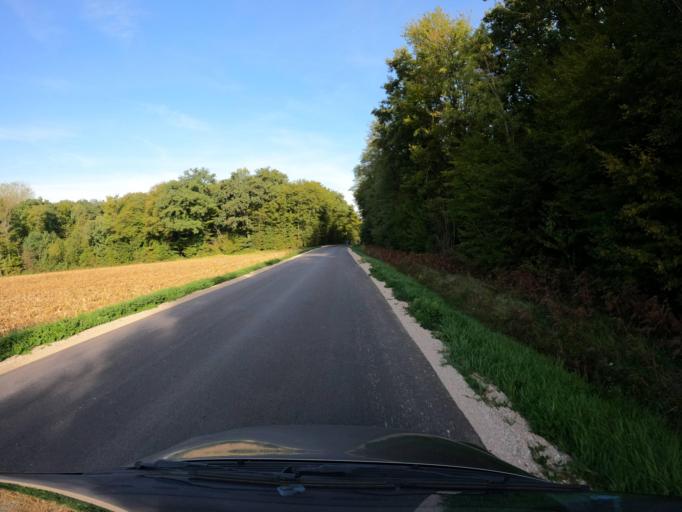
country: FR
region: Franche-Comte
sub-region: Departement du Jura
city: Montmorot
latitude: 46.7200
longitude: 5.5161
